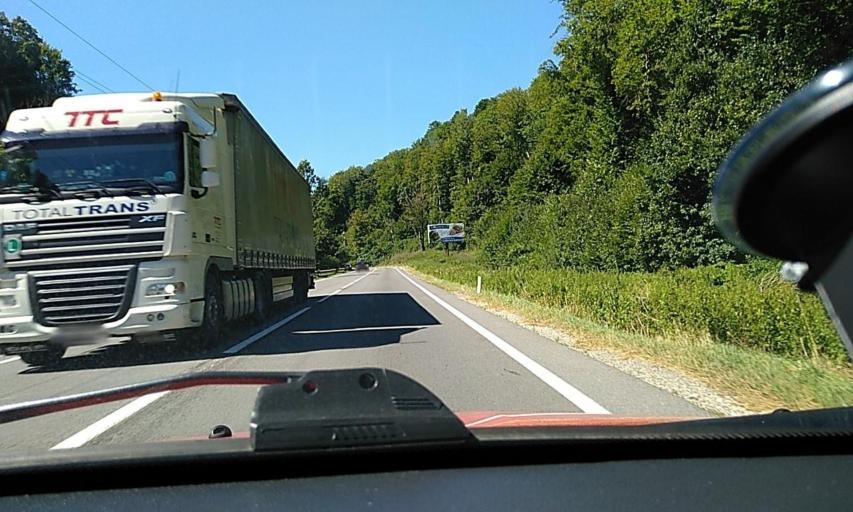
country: RO
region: Brasov
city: Maierus
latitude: 45.9031
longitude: 25.4657
